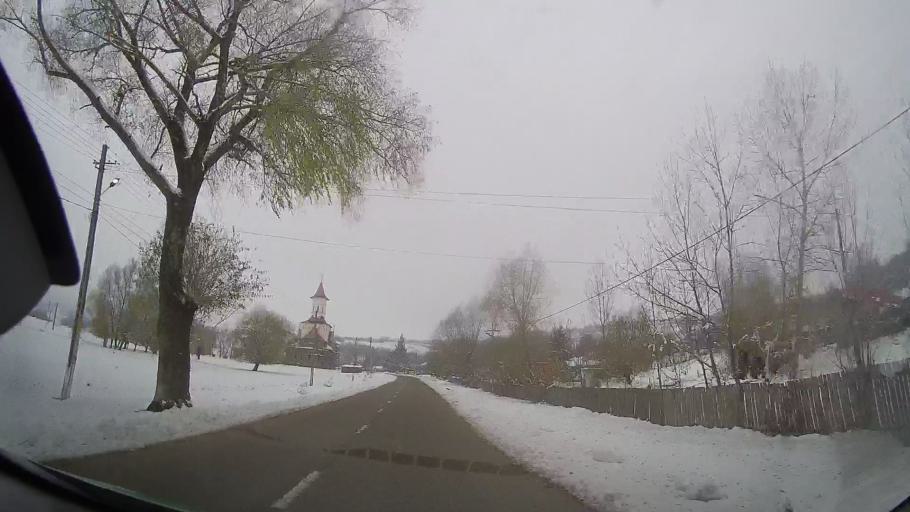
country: RO
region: Neamt
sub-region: Comuna Oniceni
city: Oniceni
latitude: 46.8063
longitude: 27.1744
